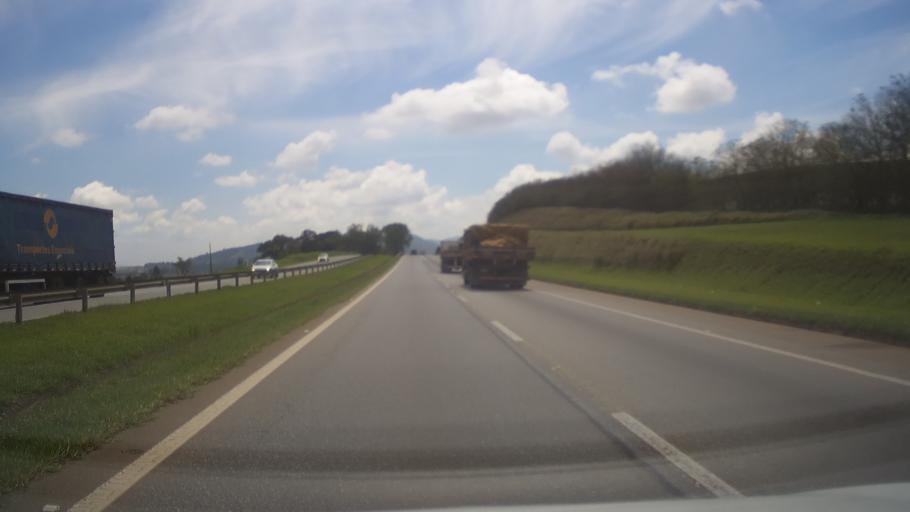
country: BR
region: Minas Gerais
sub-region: Santa Rita Do Sapucai
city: Santa Rita do Sapucai
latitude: -22.1010
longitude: -45.7220
